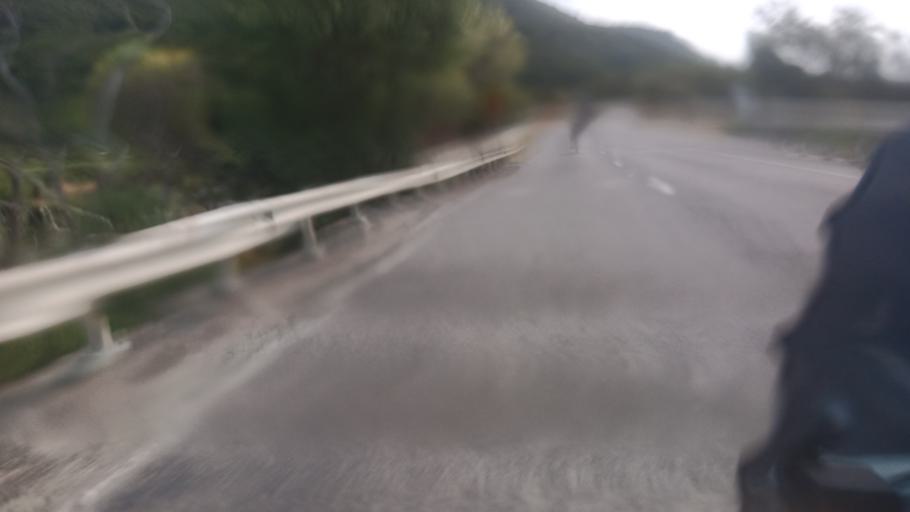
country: NZ
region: Bay of Plenty
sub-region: Opotiki District
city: Opotiki
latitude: -37.8688
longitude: 177.6021
